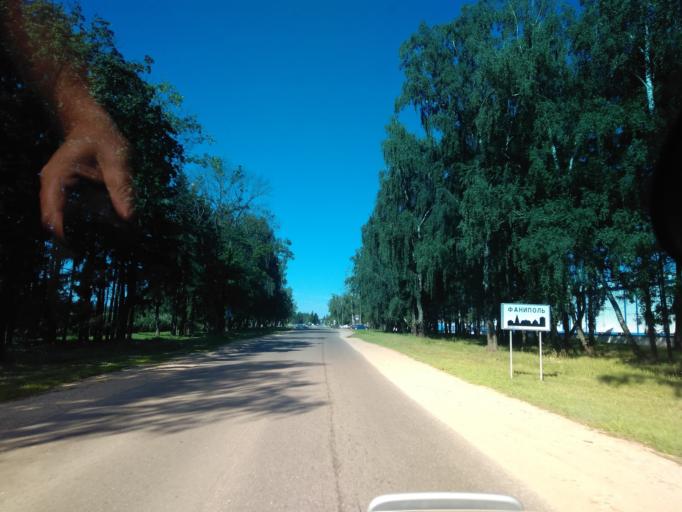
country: BY
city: Fanipol
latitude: 53.7405
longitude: 27.3608
